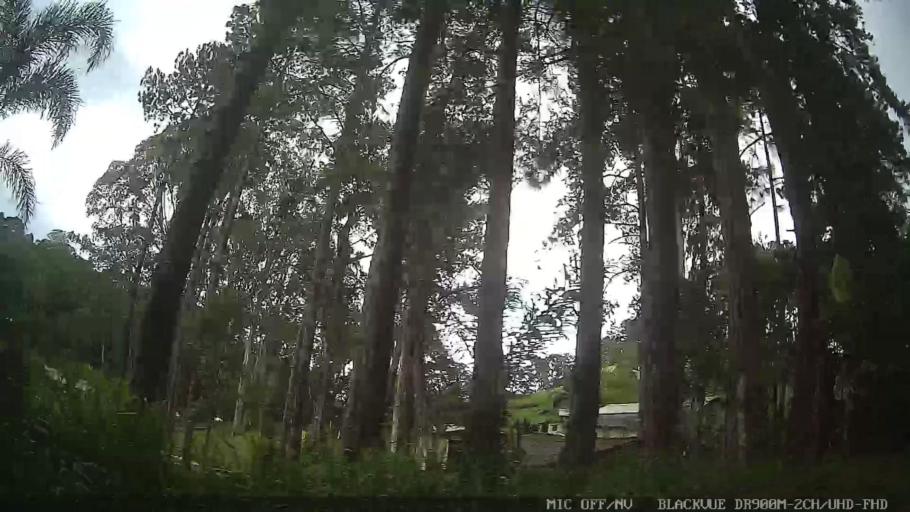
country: BR
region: Sao Paulo
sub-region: Mogi das Cruzes
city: Mogi das Cruzes
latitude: -23.4951
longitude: -46.2013
